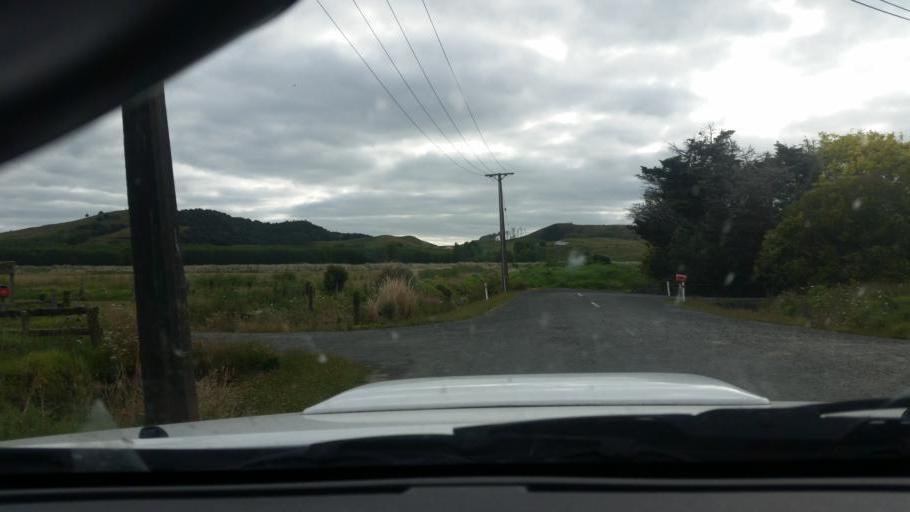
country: NZ
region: Northland
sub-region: Kaipara District
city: Dargaville
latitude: -35.9237
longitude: 173.9137
